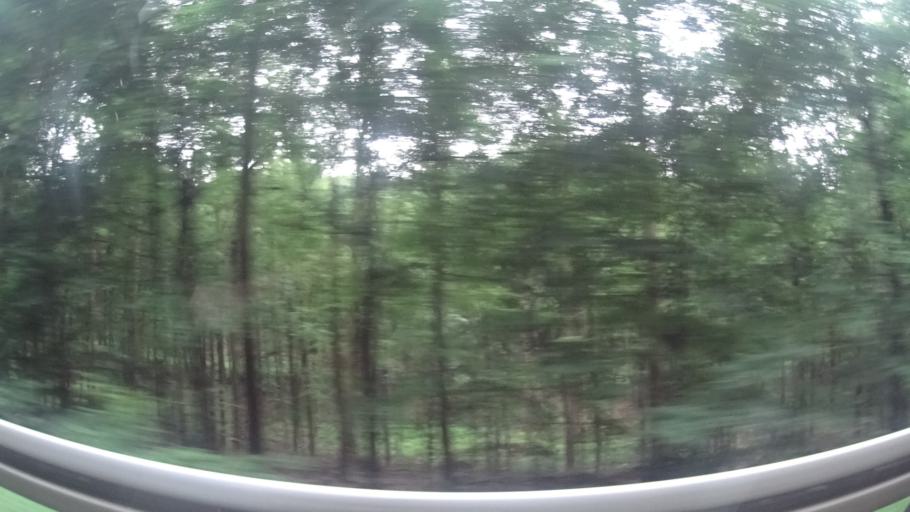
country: DE
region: Hesse
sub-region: Regierungsbezirk Darmstadt
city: Steinau an der Strasse
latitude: 50.2515
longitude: 9.4355
